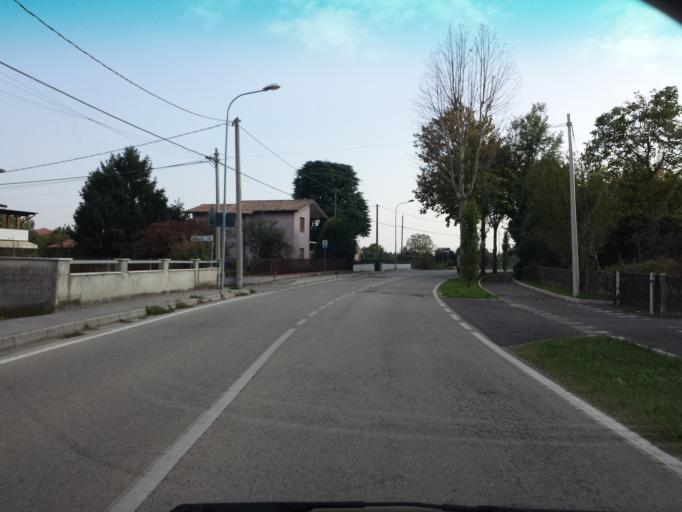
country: IT
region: Veneto
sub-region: Provincia di Vicenza
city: Dueville
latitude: 45.6246
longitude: 11.5536
